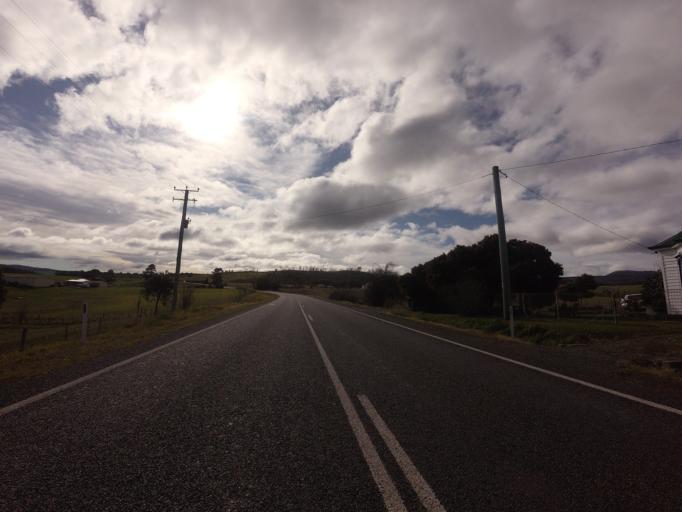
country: AU
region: Tasmania
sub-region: Derwent Valley
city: New Norfolk
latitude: -42.6618
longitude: 146.9345
